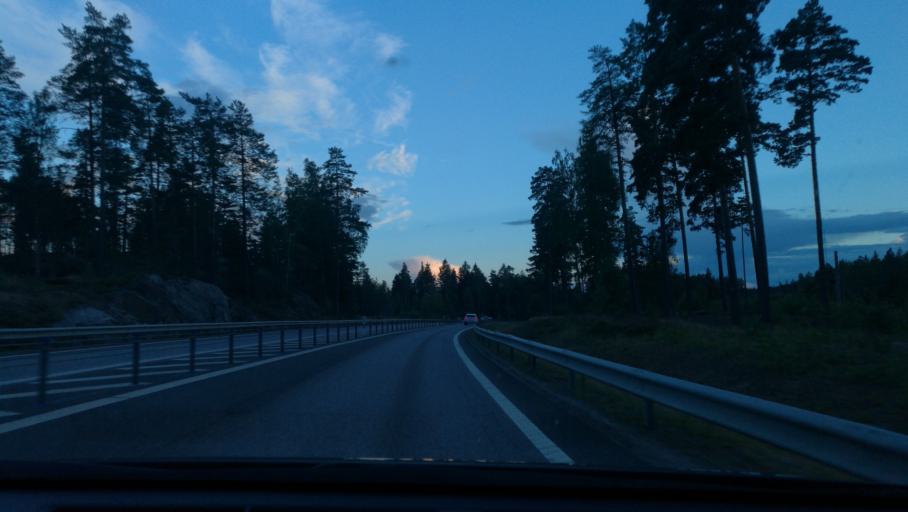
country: SE
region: Soedermanland
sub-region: Katrineholms Kommun
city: Katrineholm
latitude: 58.8337
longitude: 16.1959
